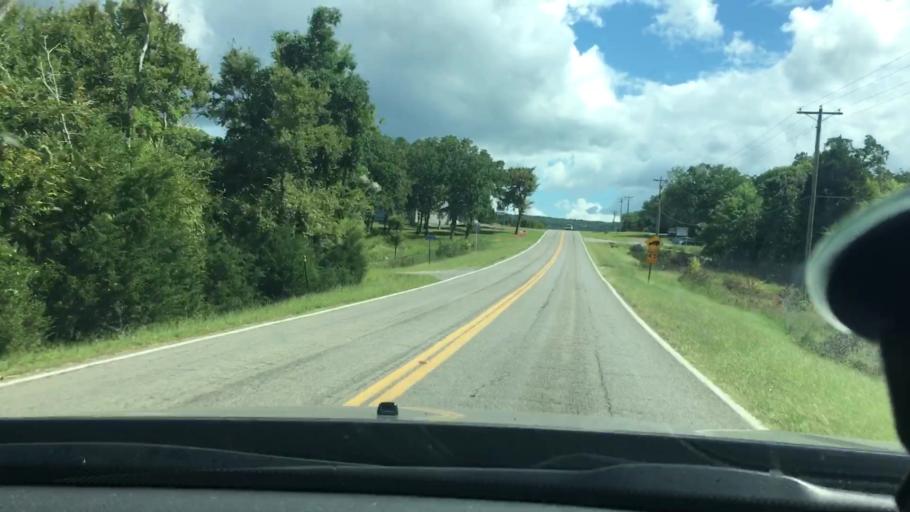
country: US
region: Oklahoma
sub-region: Cherokee County
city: Park Hill
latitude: 35.6931
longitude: -94.9136
